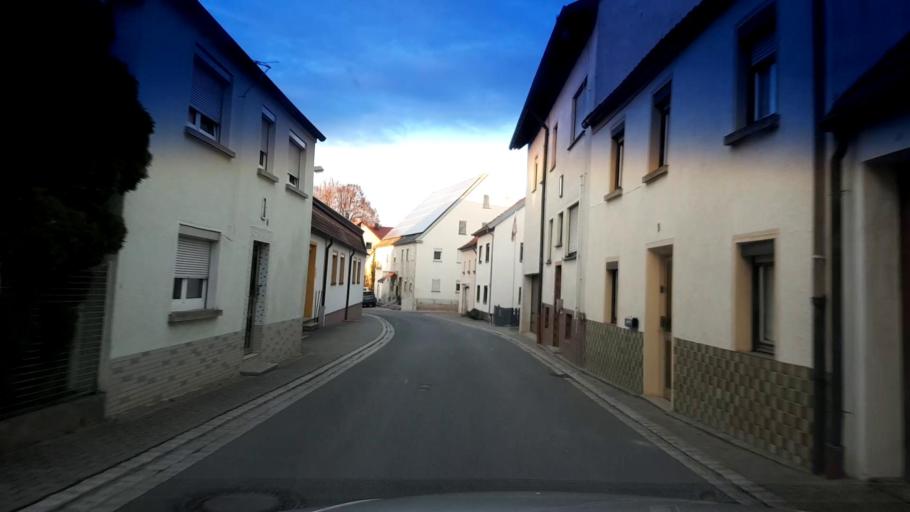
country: DE
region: Bavaria
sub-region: Upper Franconia
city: Priesendorf
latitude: 49.8814
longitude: 10.7297
